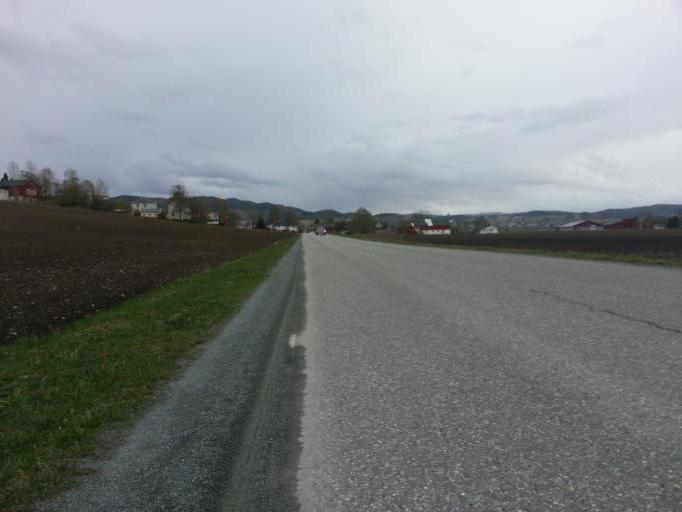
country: NO
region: Nord-Trondelag
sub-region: Levanger
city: Skogn
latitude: 63.6983
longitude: 11.1956
